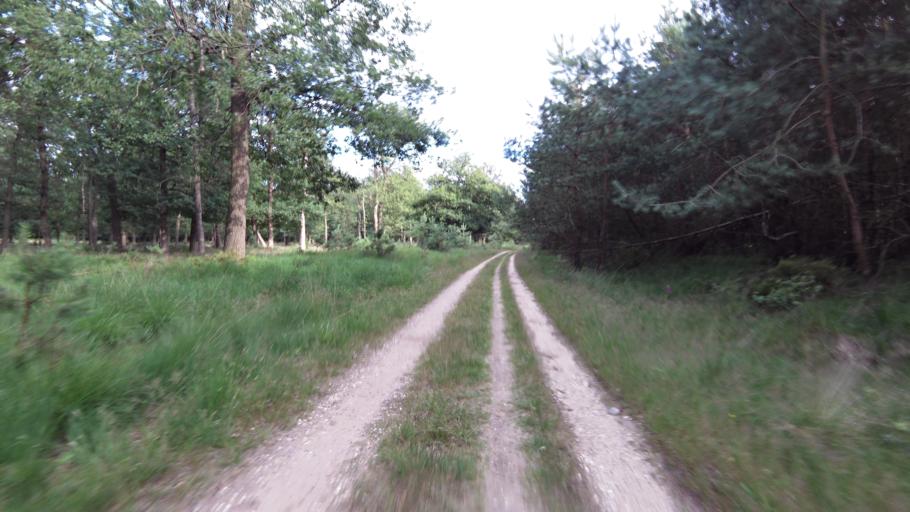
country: NL
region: Gelderland
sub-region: Gemeente Apeldoorn
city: Uddel
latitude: 52.2445
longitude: 5.8614
